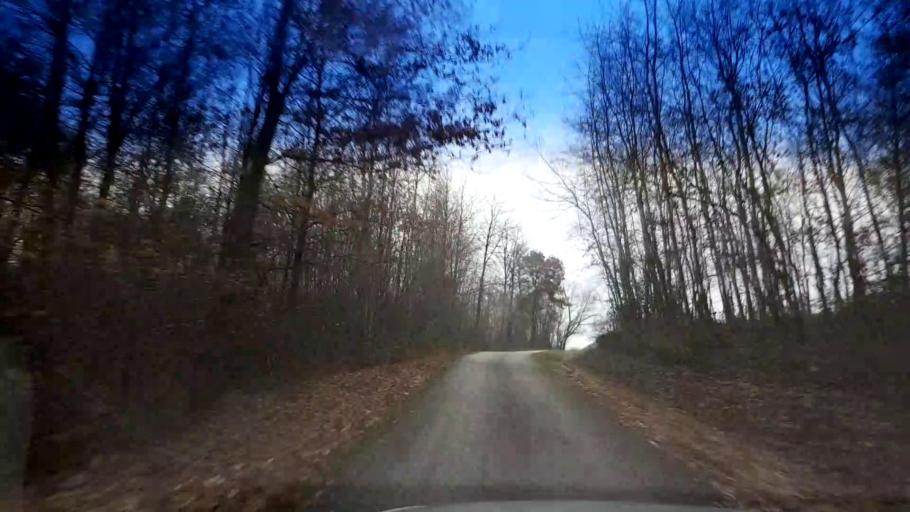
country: DE
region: Bavaria
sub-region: Upper Franconia
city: Zapfendorf
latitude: 49.9968
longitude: 10.9436
